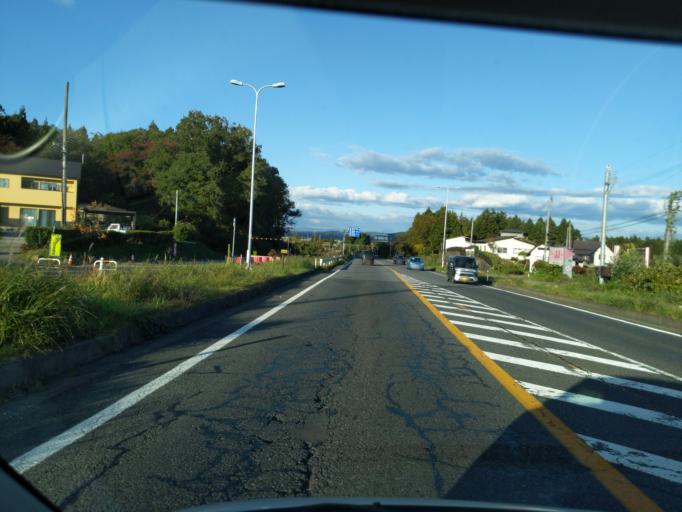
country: JP
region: Iwate
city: Kitakami
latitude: 39.2367
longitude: 141.0953
